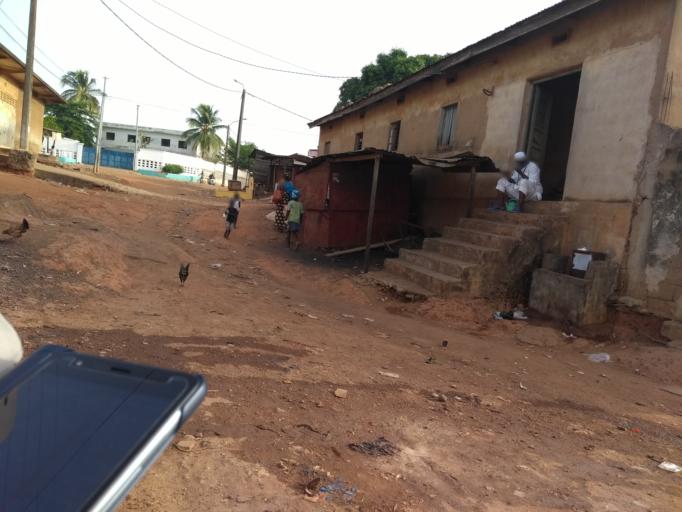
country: CI
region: Vallee du Bandama
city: Bouake
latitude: 7.7080
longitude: -5.0267
